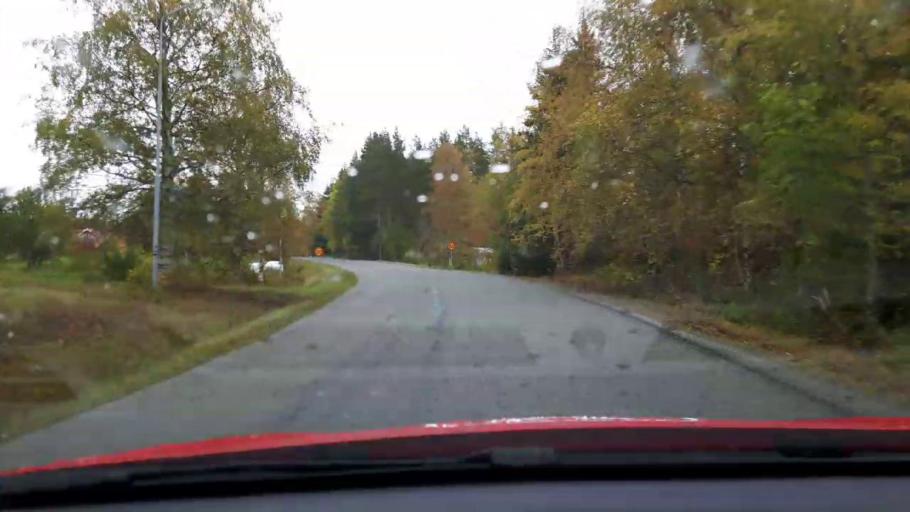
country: SE
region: Jaemtland
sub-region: Bergs Kommun
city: Hoverberg
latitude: 62.9375
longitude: 14.5081
